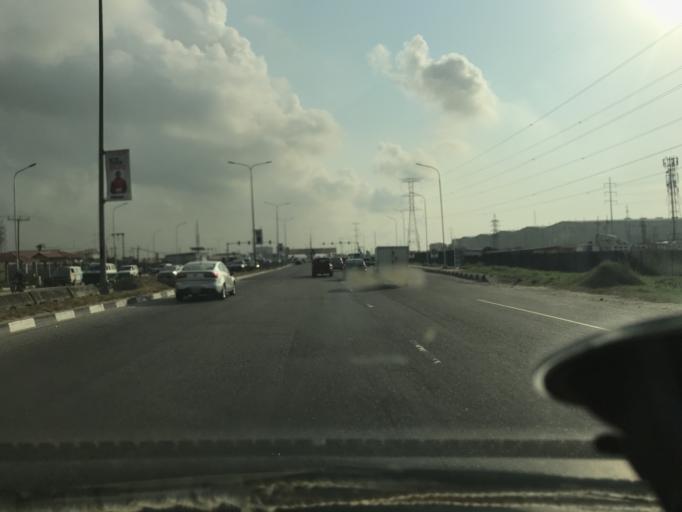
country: NG
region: Lagos
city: Ikoyi
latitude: 6.4327
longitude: 3.4804
